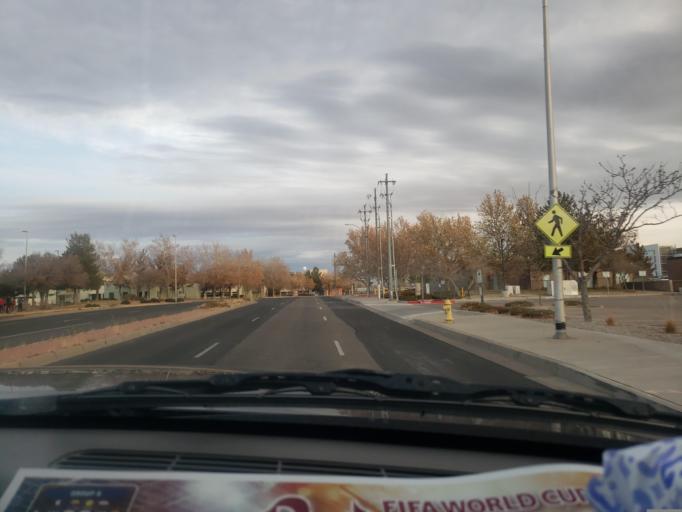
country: US
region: New Mexico
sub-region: Bernalillo County
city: Albuquerque
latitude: 35.0701
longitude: -106.6309
